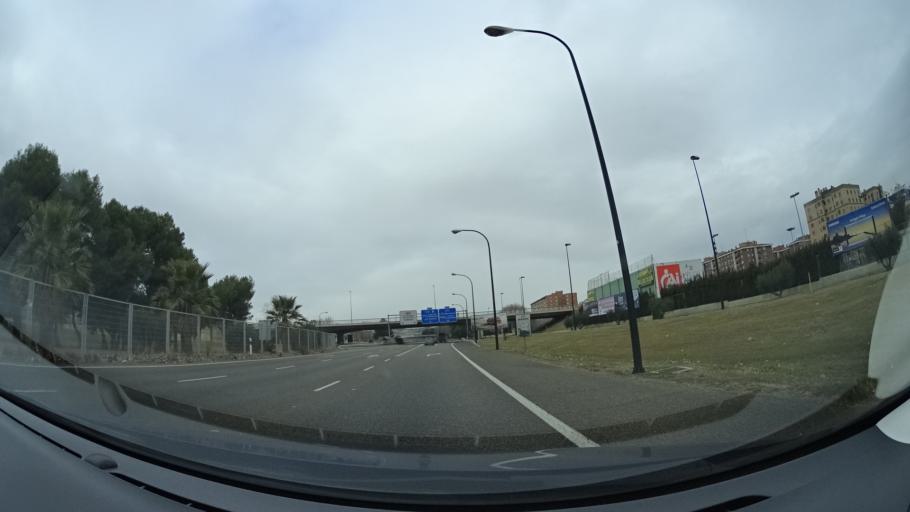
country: ES
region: Aragon
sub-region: Provincia de Zaragoza
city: Zaragoza
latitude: 41.6717
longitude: -0.8803
